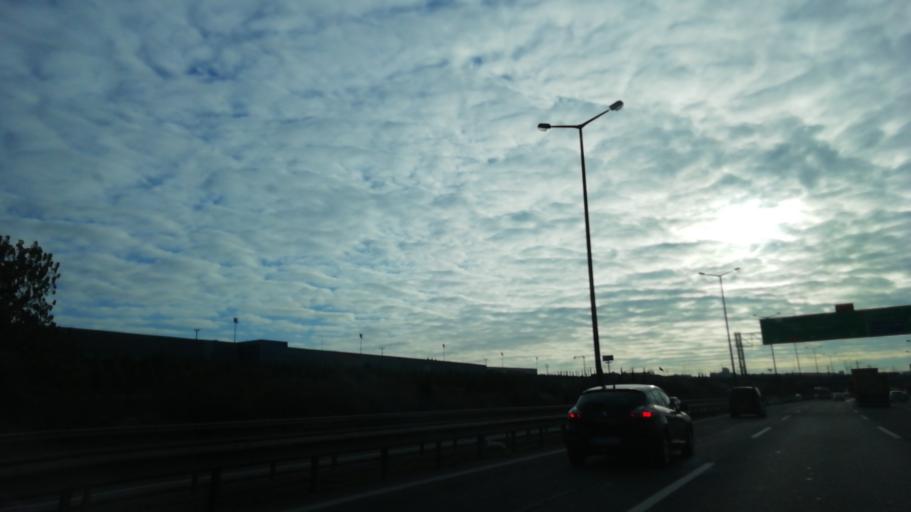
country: TR
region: Kocaeli
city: Balcik
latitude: 40.8734
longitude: 29.3926
